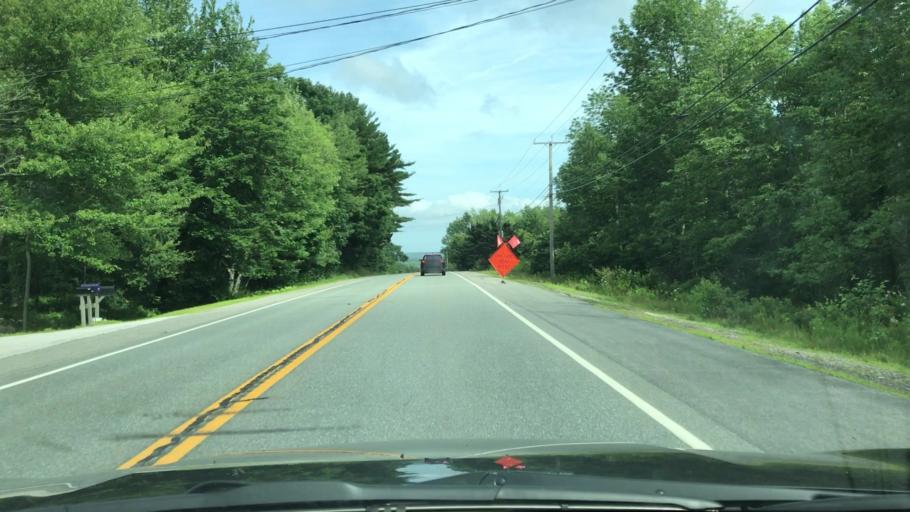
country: US
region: Maine
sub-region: Hancock County
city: Surry
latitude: 44.5437
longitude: -68.5125
